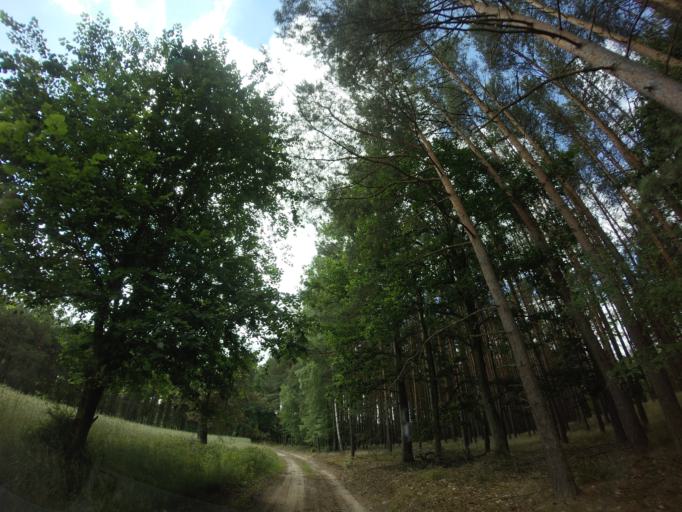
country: PL
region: Lubusz
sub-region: Powiat strzelecko-drezdenecki
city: Dobiegniew
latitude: 53.0062
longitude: 15.7130
